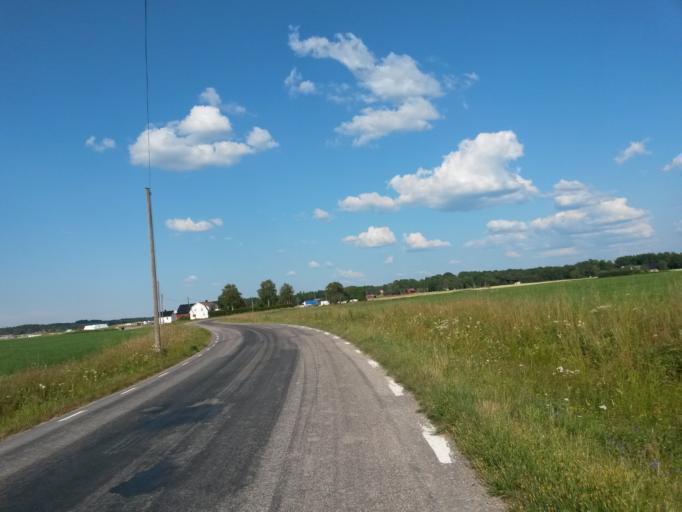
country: SE
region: Vaestra Goetaland
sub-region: Vargarda Kommun
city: Jonstorp
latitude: 58.0116
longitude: 12.6878
